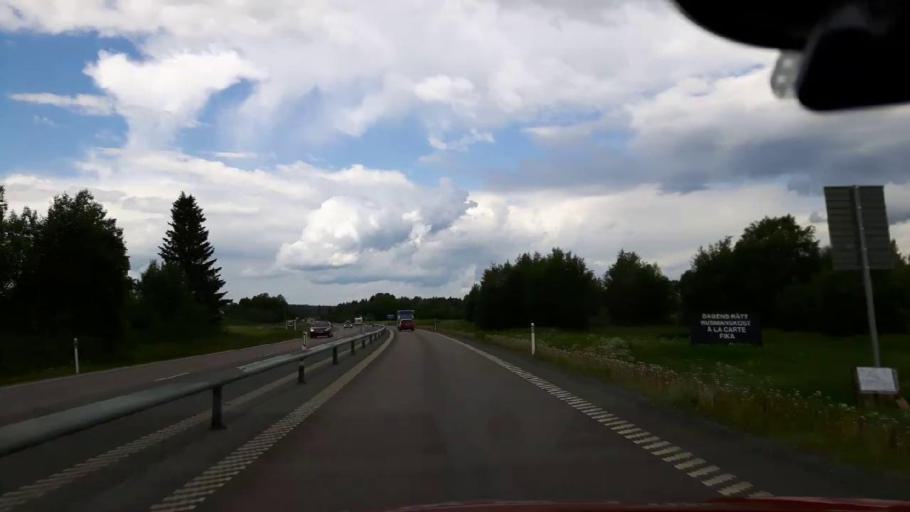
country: SE
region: Jaemtland
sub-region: Krokoms Kommun
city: Krokom
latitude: 63.3100
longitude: 14.4809
